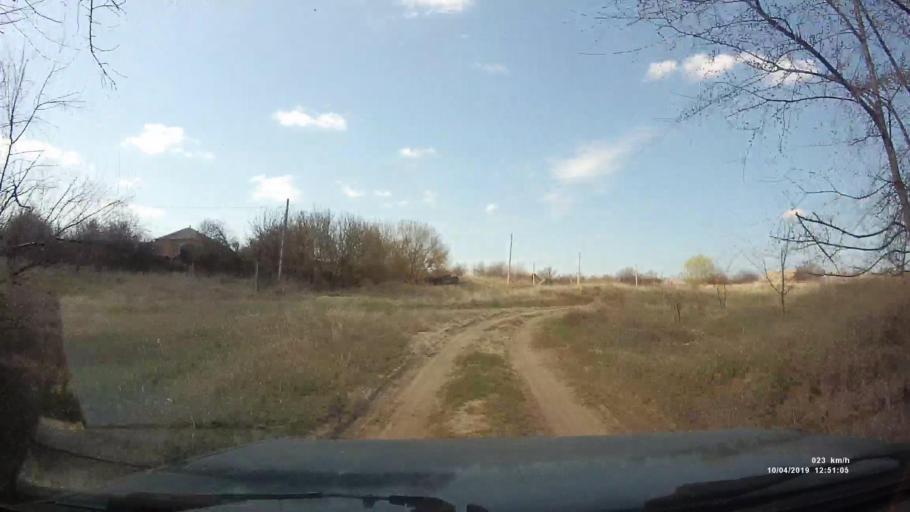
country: RU
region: Rostov
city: Kamensk-Shakhtinskiy
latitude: 48.3587
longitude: 40.2187
